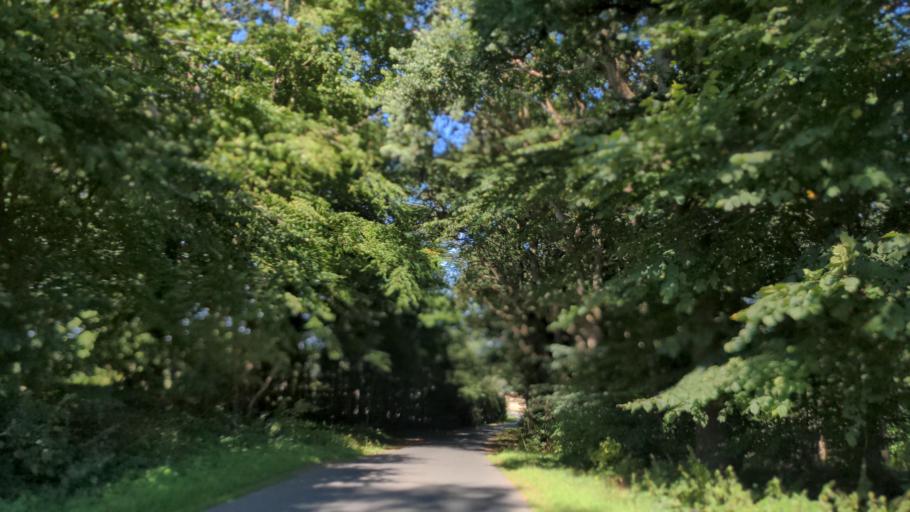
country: DE
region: Schleswig-Holstein
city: Gross Disnack
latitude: 53.7465
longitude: 10.6915
